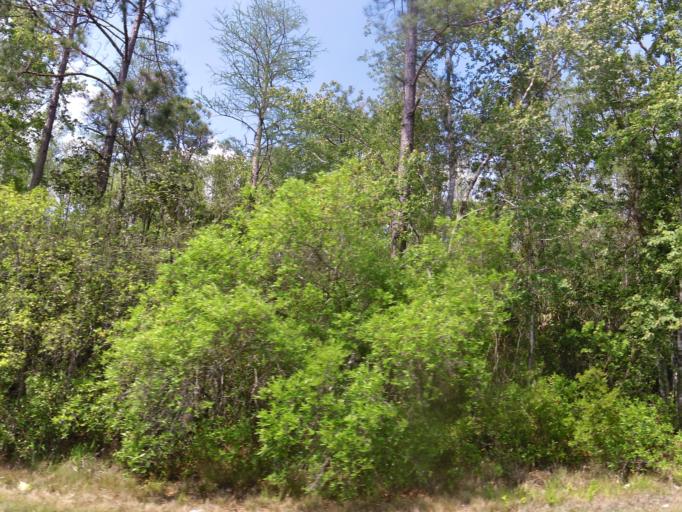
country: US
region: Georgia
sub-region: Camden County
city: Kingsland
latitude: 30.8105
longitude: -81.7740
